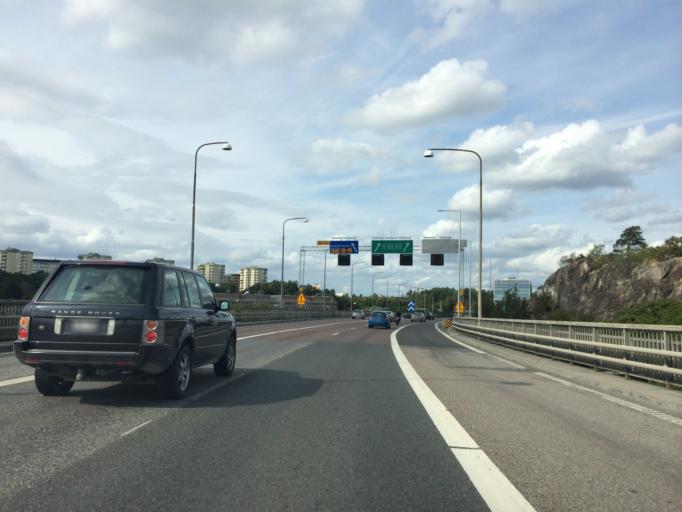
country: SE
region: Stockholm
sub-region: Solna Kommun
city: Solna
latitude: 59.3425
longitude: 18.0100
